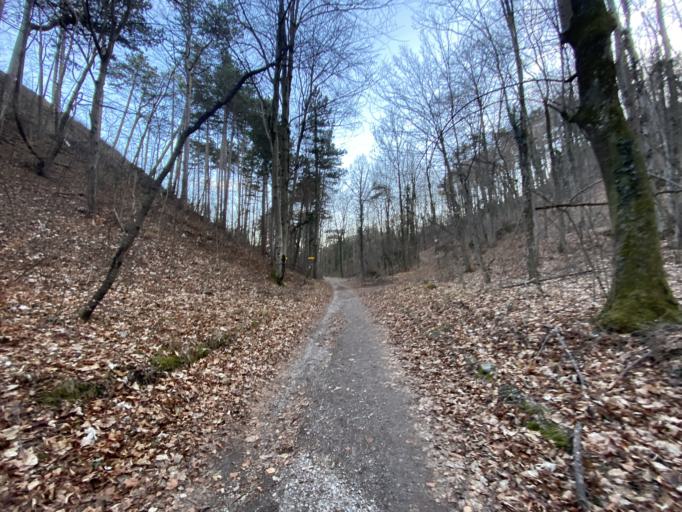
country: AT
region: Lower Austria
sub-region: Politischer Bezirk Baden
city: Hirtenberg
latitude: 47.9764
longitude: 16.1542
